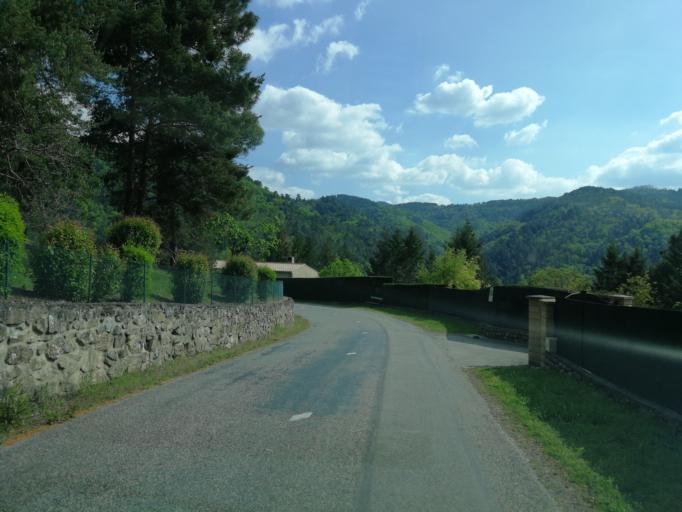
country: FR
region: Rhone-Alpes
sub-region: Departement de l'Ardeche
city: Saint-Sauveur-de-Montagut
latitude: 44.8080
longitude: 4.6202
